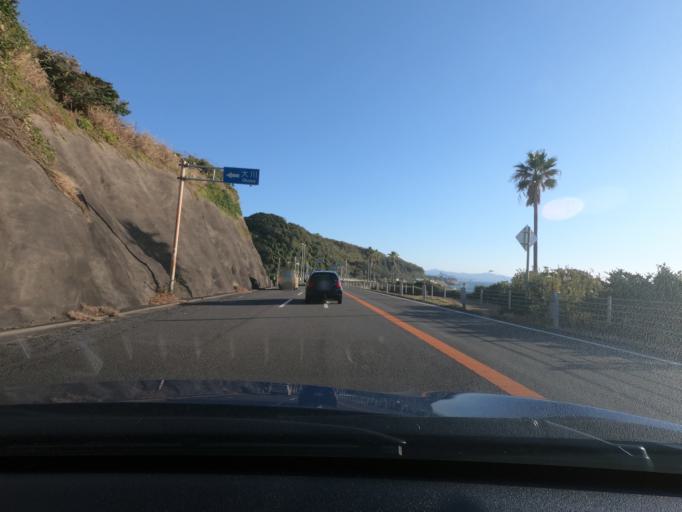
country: JP
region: Kagoshima
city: Akune
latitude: 31.9503
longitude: 130.2159
